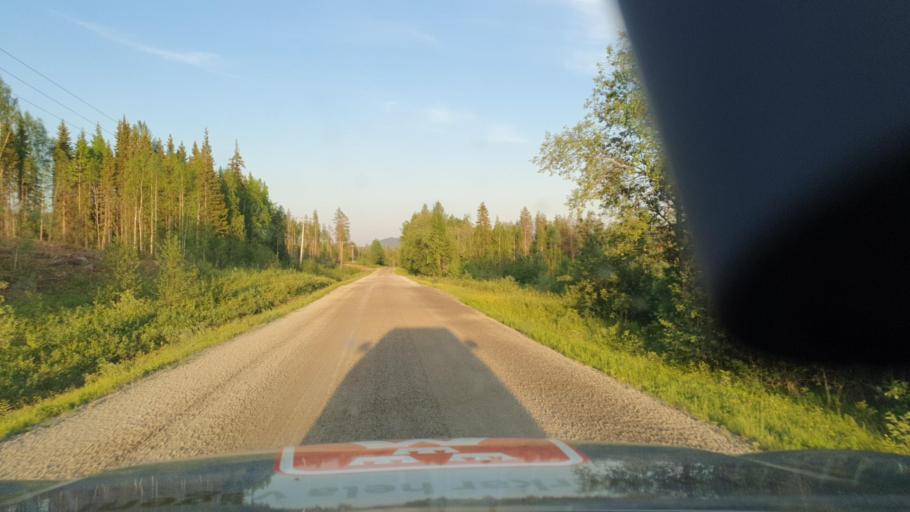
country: SE
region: Norrbotten
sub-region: Bodens Kommun
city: Boden
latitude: 66.1730
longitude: 21.5226
